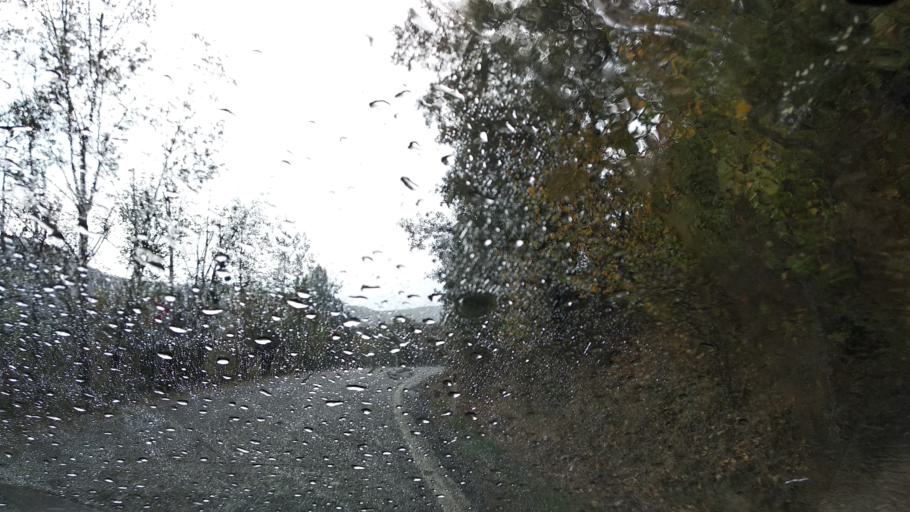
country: TR
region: Ankara
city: Nallihan
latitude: 40.3287
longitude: 31.4102
